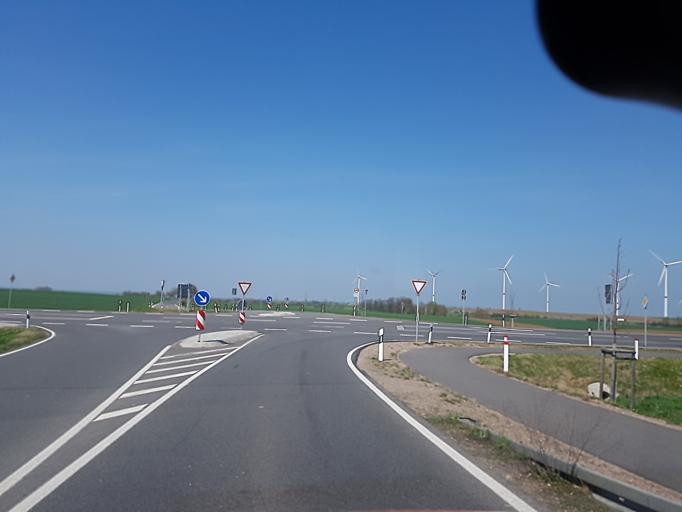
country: DE
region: Saxony
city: Mutzschen
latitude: 51.2395
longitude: 12.8457
